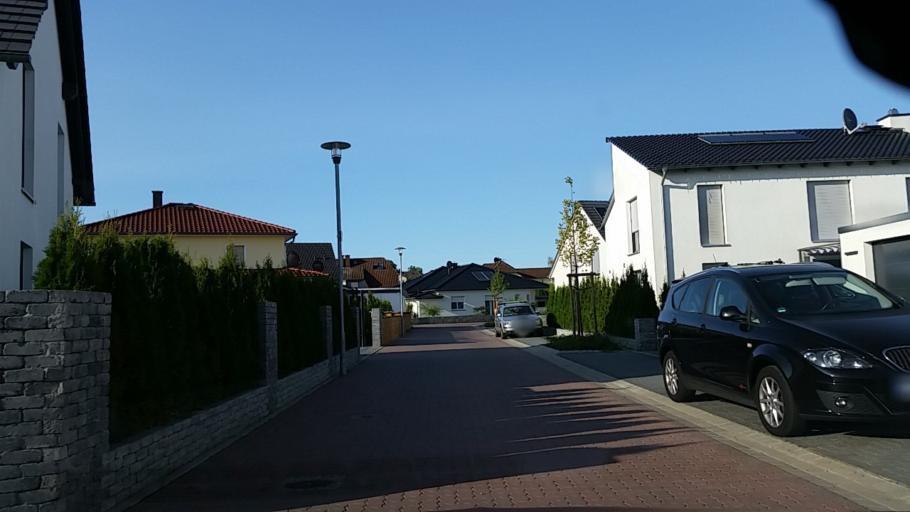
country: DE
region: Lower Saxony
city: Lehre
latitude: 52.3211
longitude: 10.6732
